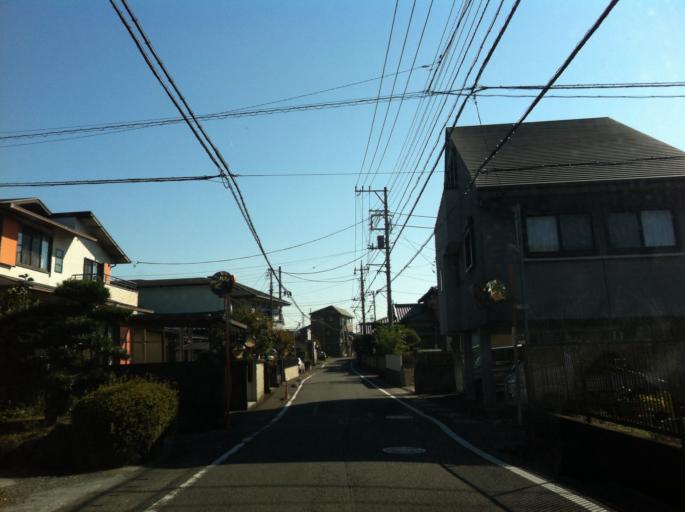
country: JP
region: Shizuoka
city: Fuji
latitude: 35.1582
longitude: 138.7493
